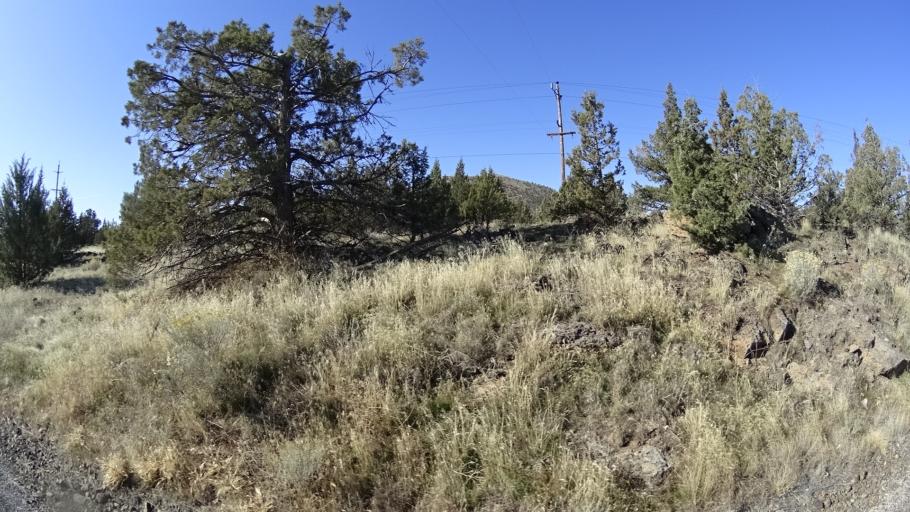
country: US
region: California
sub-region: Siskiyou County
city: Montague
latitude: 41.6732
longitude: -122.3696
